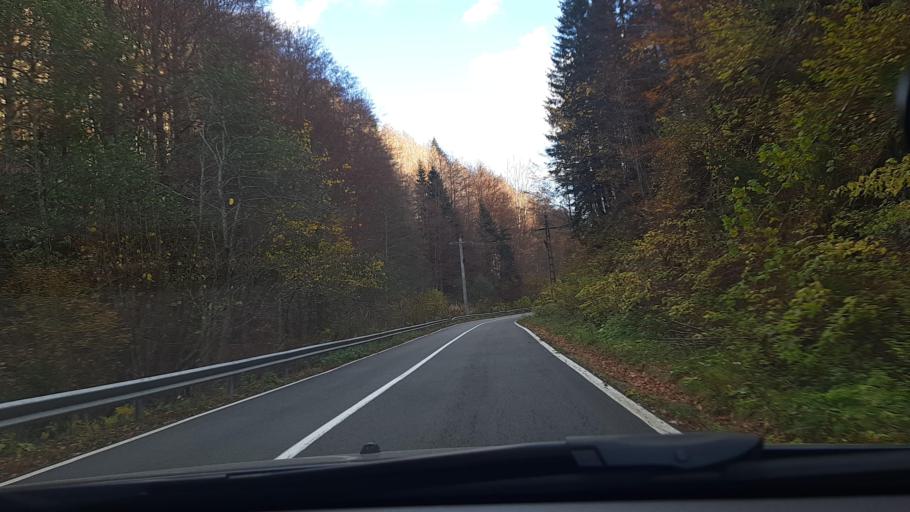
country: RO
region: Valcea
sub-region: Comuna Voineasa
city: Voineasa
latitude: 45.4368
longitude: 23.8744
